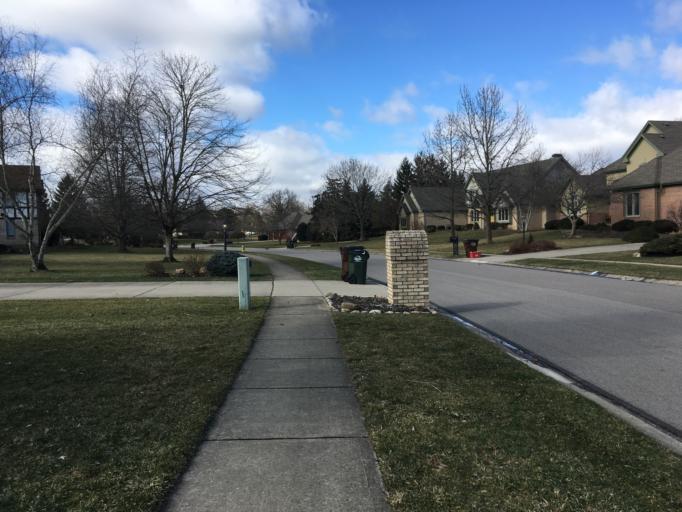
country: US
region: Ohio
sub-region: Montgomery County
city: Centerville
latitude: 39.5937
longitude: -84.1490
